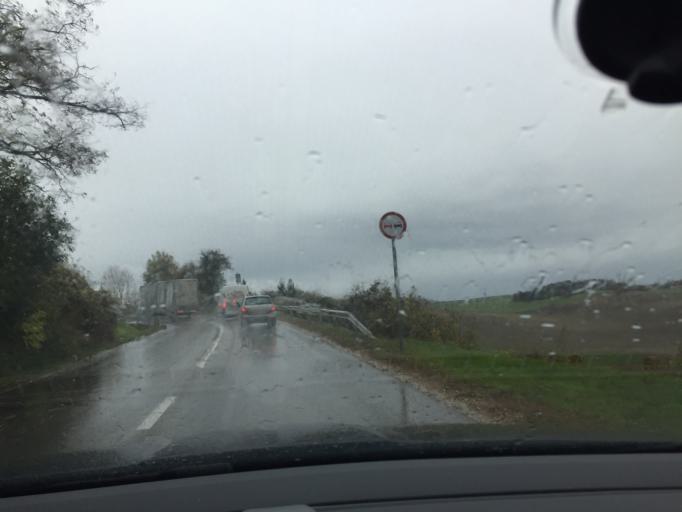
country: HU
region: Komarom-Esztergom
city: Bajna
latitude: 47.6589
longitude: 18.5923
